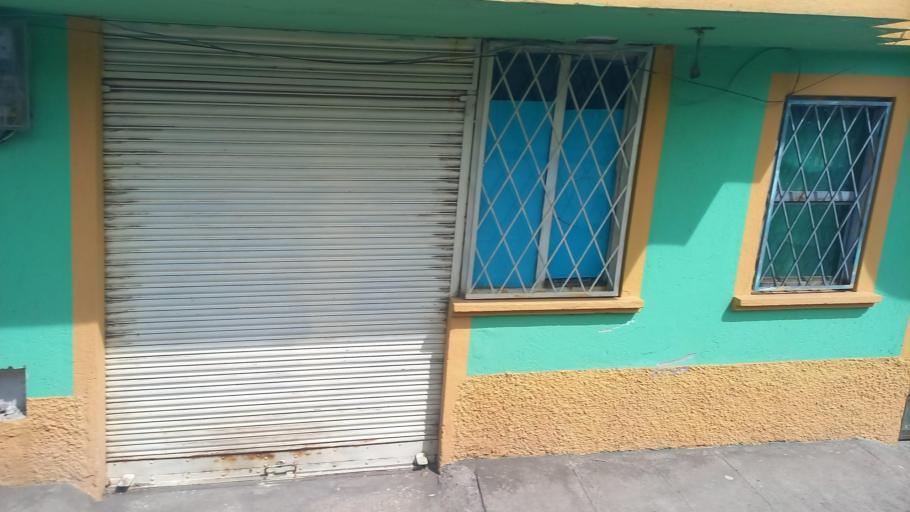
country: EC
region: Pichincha
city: Cayambe
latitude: 0.1421
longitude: -78.0727
